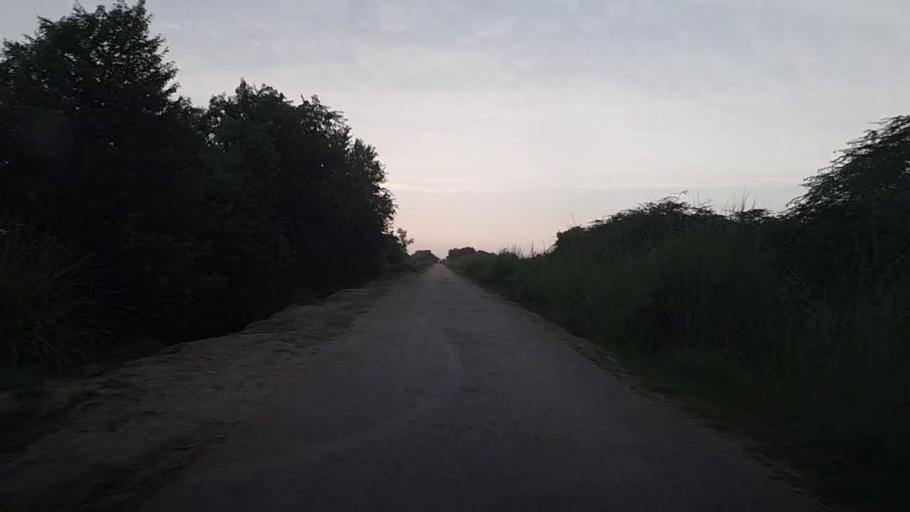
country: PK
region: Sindh
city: Karaundi
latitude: 27.0168
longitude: 68.3528
